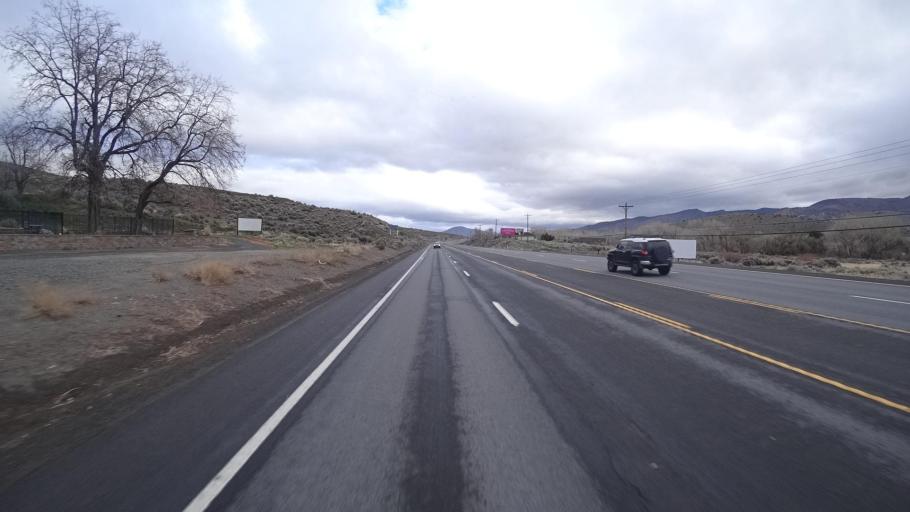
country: US
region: Nevada
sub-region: Storey County
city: Virginia City
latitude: 39.3733
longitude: -119.7463
